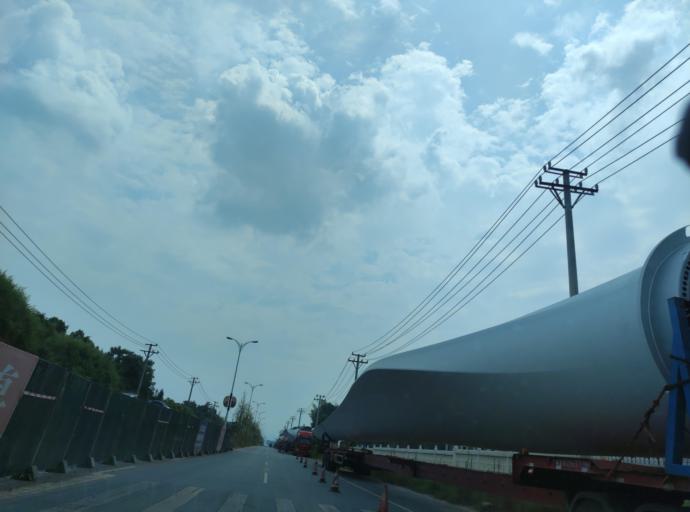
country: CN
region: Jiangxi Sheng
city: Yuannan
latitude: 27.6640
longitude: 114.0251
